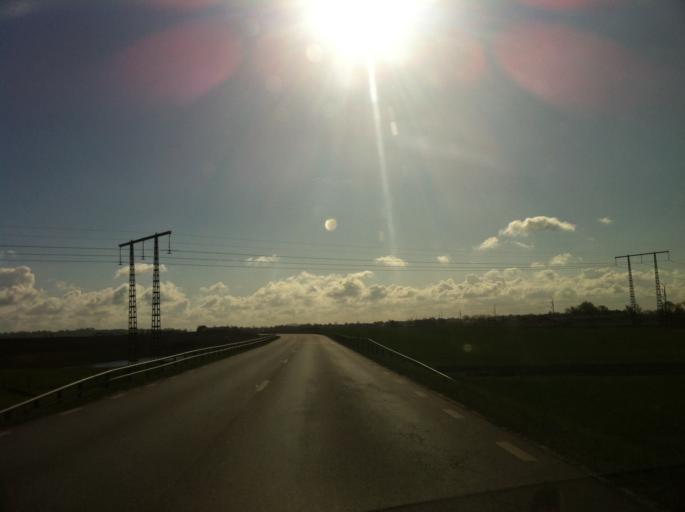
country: SE
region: Skane
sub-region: Svalovs Kommun
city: Teckomatorp
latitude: 55.8742
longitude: 13.0909
